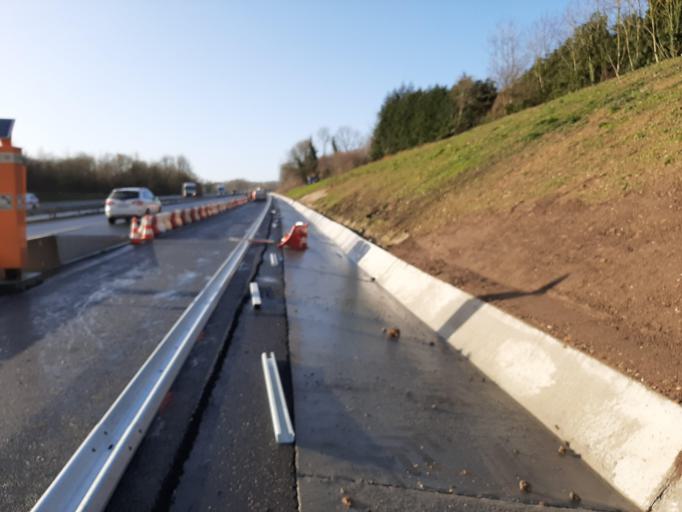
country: FR
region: Haute-Normandie
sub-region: Departement de l'Eure
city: Beuzeville
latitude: 49.3024
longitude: 0.2727
